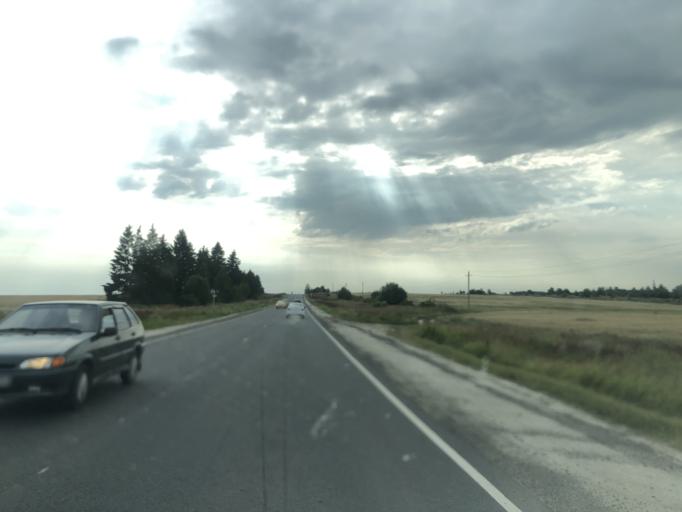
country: RU
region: Ivanovo
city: Shuya
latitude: 56.8608
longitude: 41.4507
